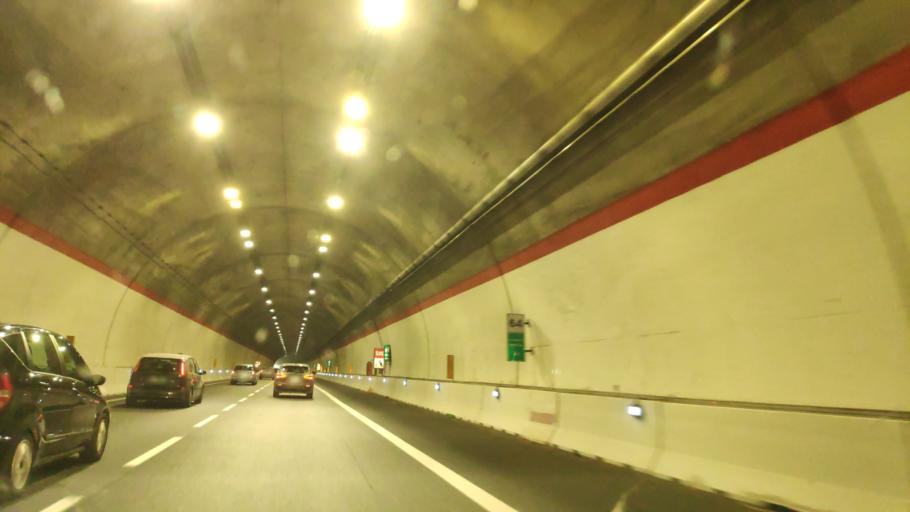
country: IT
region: Campania
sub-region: Provincia di Salerno
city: Sicignano degli Alburni
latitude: 40.5790
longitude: 15.3445
